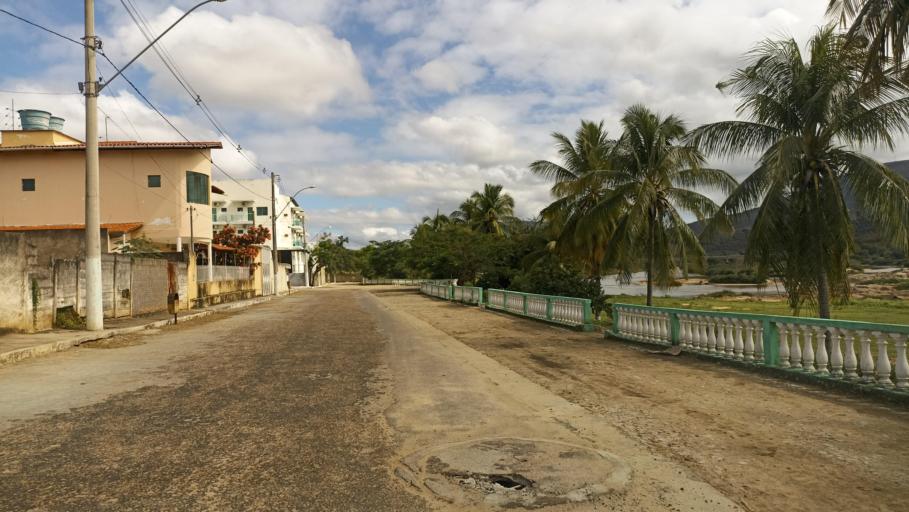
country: BR
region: Minas Gerais
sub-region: Jequitinhonha
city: Jequitinhonha
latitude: -16.4317
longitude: -41.0041
